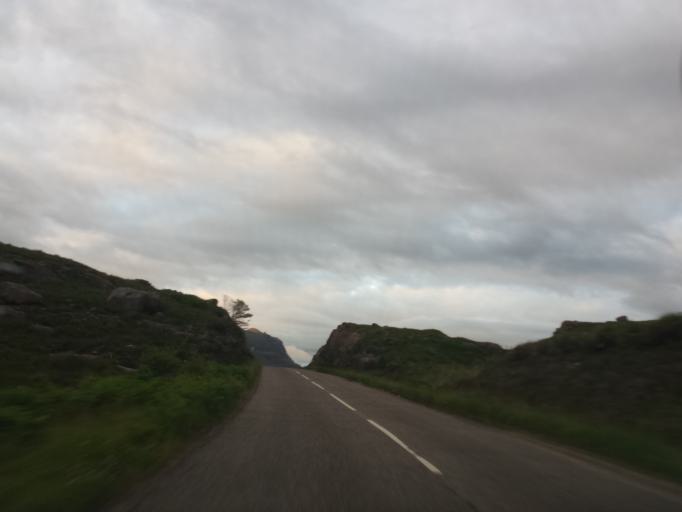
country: GB
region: Scotland
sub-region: Highland
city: Ullapool
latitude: 57.5270
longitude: -5.5684
